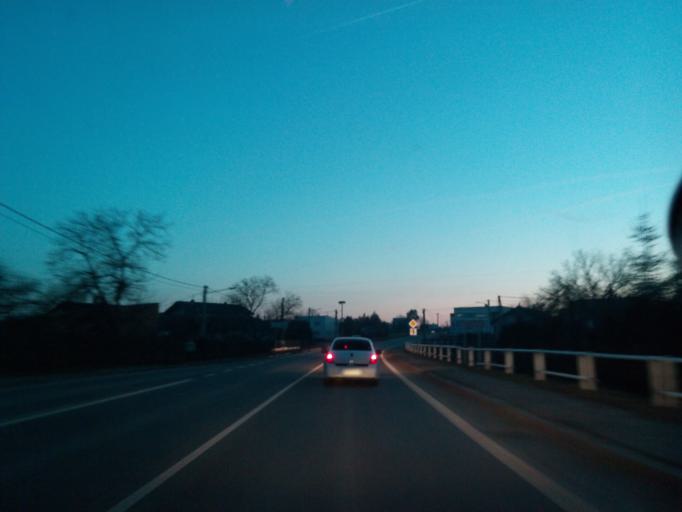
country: SK
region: Kosicky
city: Michalovce
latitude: 48.7241
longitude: 21.8540
